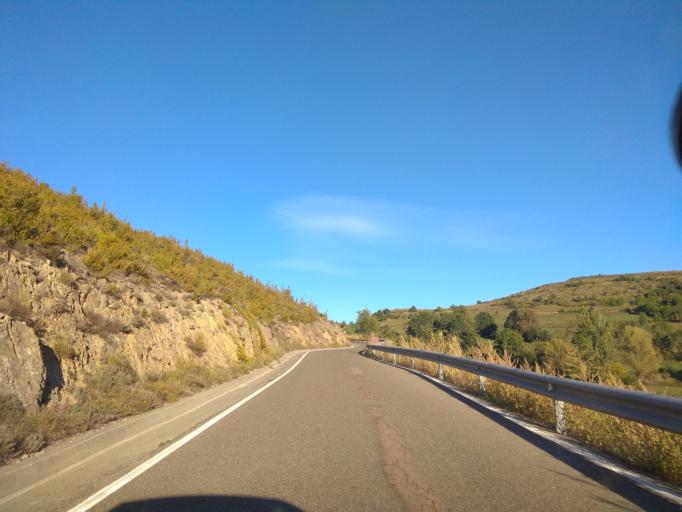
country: ES
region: Catalonia
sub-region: Provincia de Lleida
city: Lles de Cerdanya
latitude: 42.3505
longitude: 1.6896
